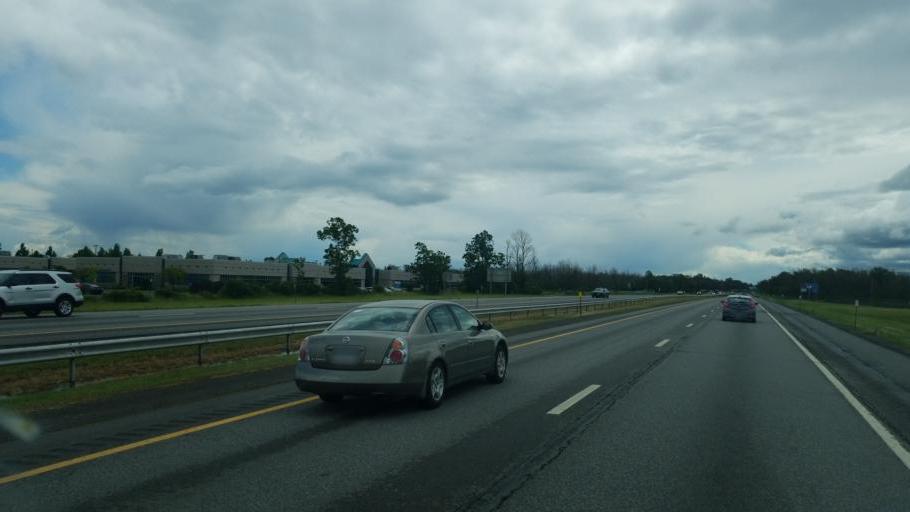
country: US
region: New York
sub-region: Erie County
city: Williamsville
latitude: 42.9506
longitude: -78.7214
